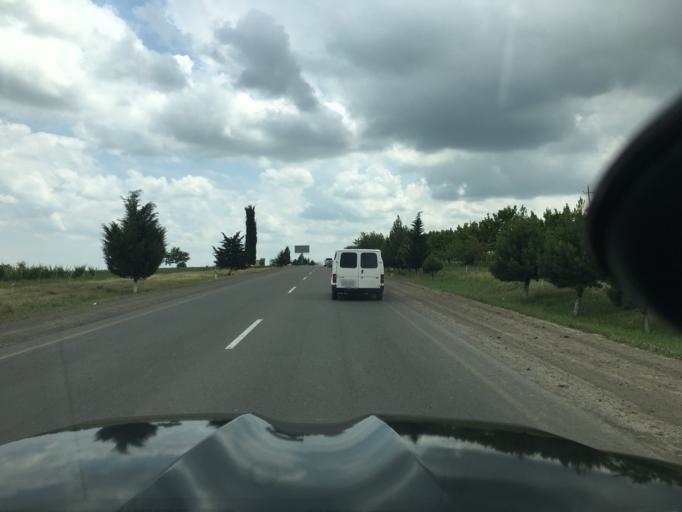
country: AZ
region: Tovuz
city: Tovuz
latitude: 40.9731
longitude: 45.6814
